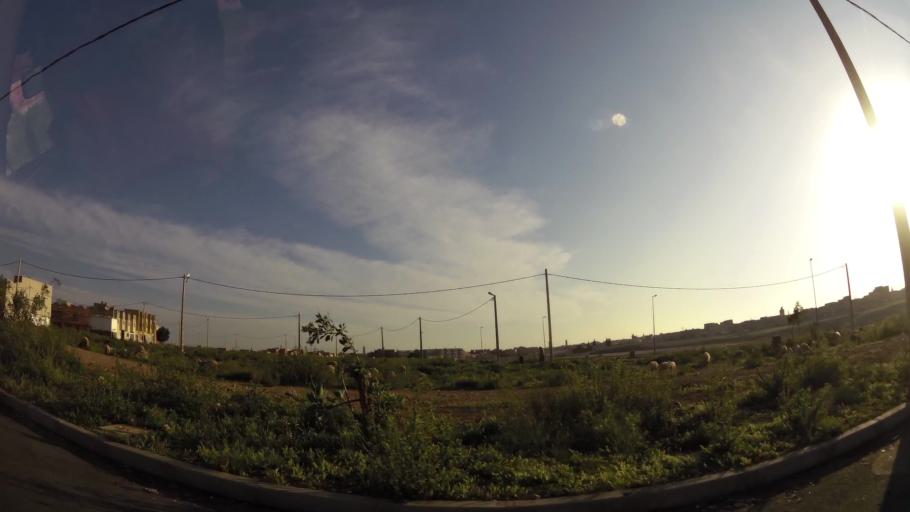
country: MA
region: Oriental
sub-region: Oujda-Angad
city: Oujda
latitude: 34.7082
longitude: -1.9023
